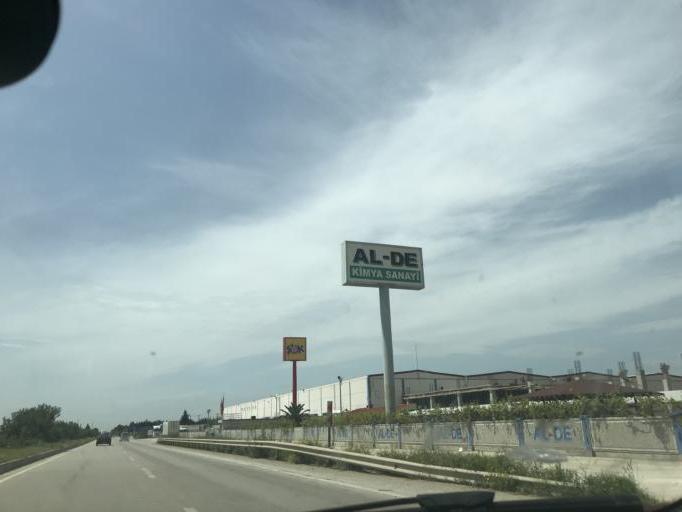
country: TR
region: Adana
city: Yakapinar
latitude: 36.9705
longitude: 35.5285
